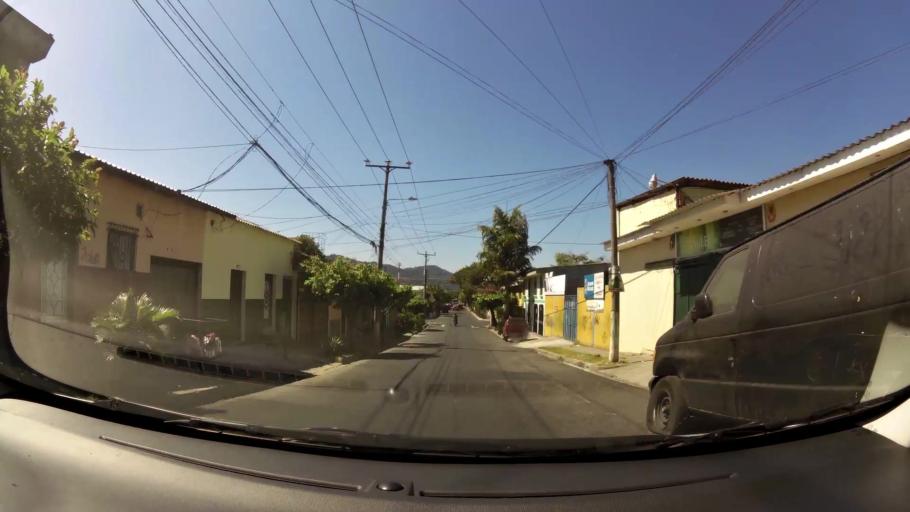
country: SV
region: La Libertad
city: Santa Tecla
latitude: 13.6767
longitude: -89.2919
